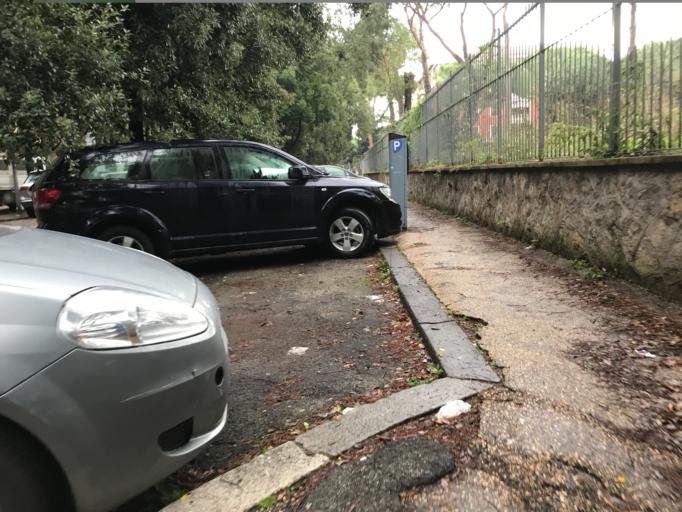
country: IT
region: Latium
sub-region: Citta metropolitana di Roma Capitale
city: Rome
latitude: 41.9129
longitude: 12.5155
